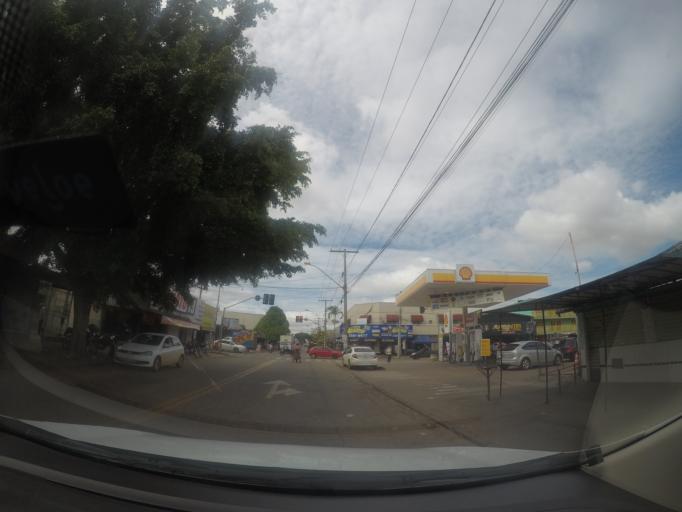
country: BR
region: Goias
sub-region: Goiania
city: Goiania
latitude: -16.6626
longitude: -49.3029
